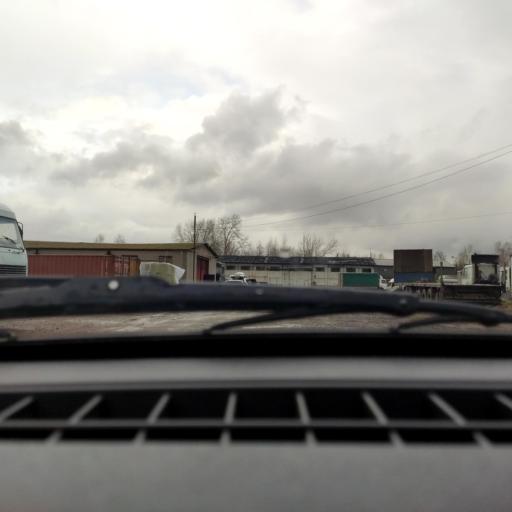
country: RU
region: Bashkortostan
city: Ufa
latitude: 54.8399
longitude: 56.1299
